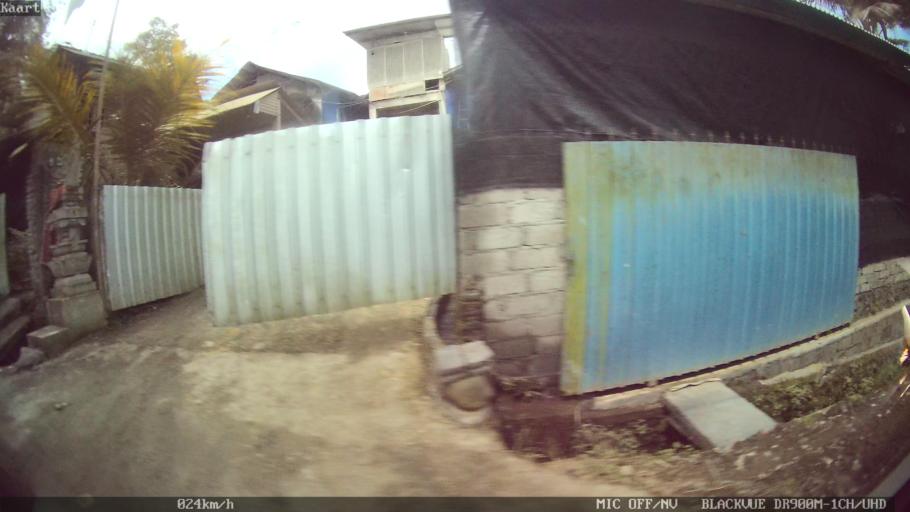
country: ID
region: Bali
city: Banjar Petak
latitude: -8.4465
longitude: 115.3278
